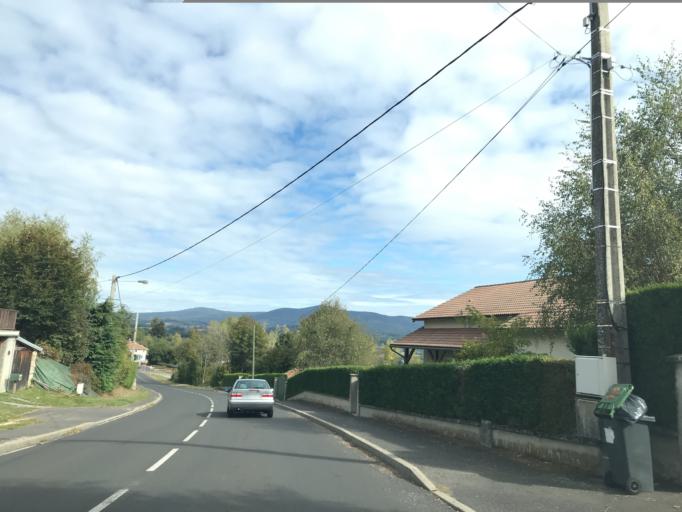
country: FR
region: Auvergne
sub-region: Departement du Puy-de-Dome
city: Celles-sur-Durolle
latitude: 45.8559
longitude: 3.6377
